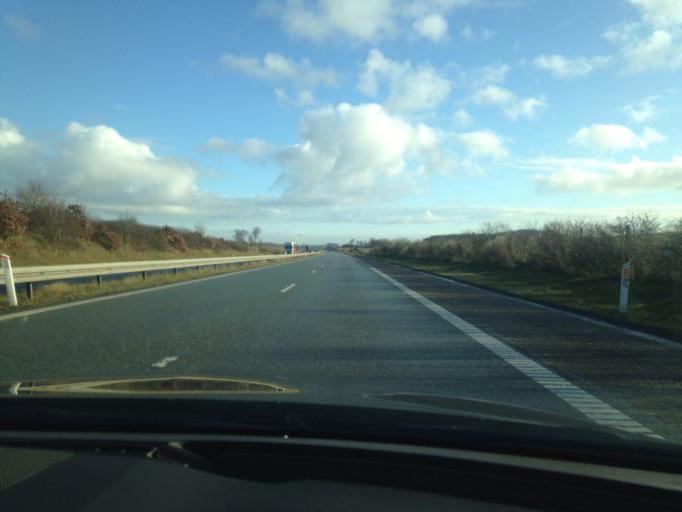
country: DK
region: South Denmark
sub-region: Vejen Kommune
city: Holsted
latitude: 55.5111
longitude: 8.9674
